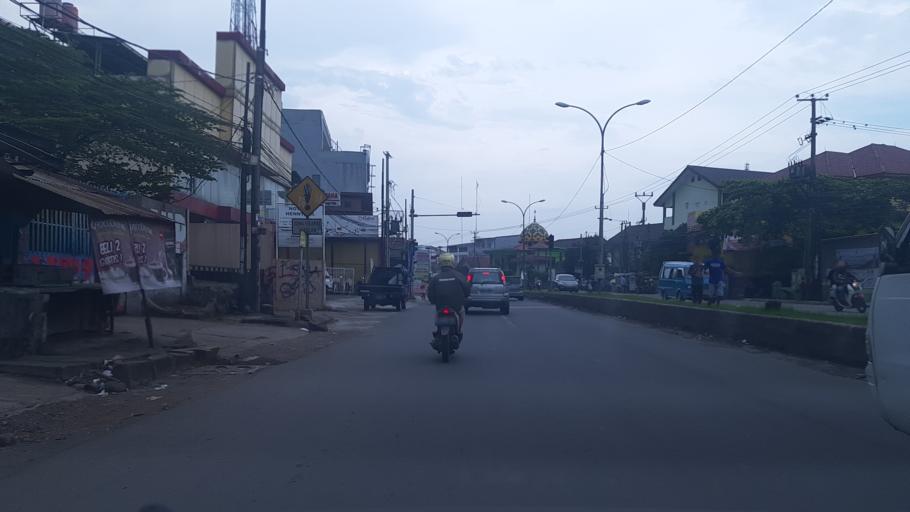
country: ID
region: West Java
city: Cibinong
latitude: -6.4710
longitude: 106.8618
